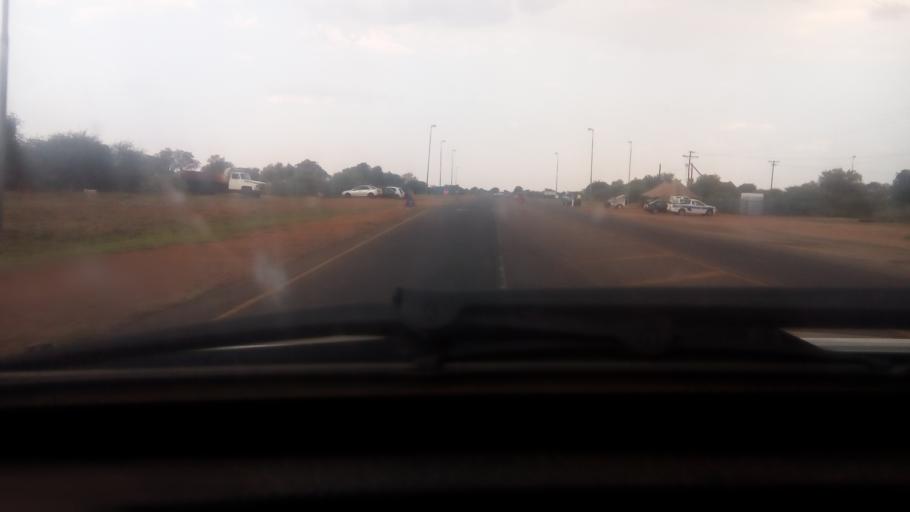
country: BW
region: Kweneng
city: Metsemotlhaba
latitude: -24.4753
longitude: 25.7143
